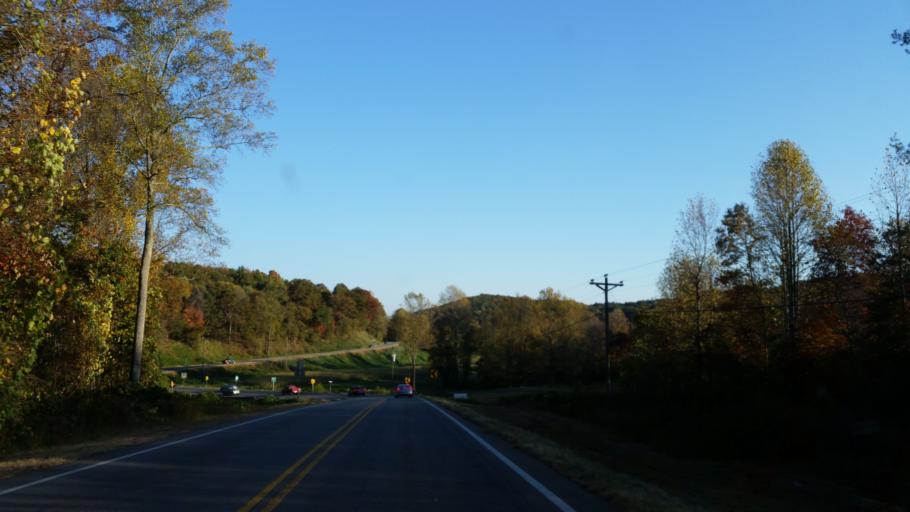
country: US
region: Georgia
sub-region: Pickens County
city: Jasper
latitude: 34.5397
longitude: -84.2661
